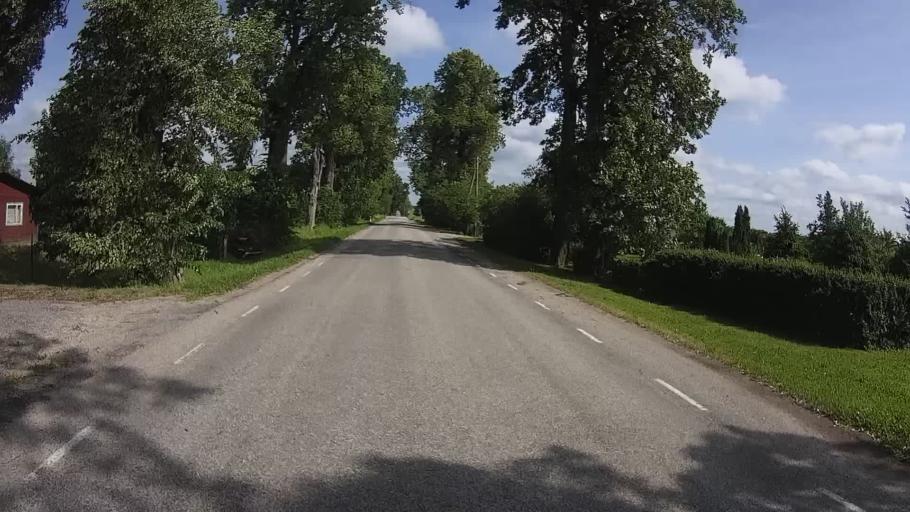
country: EE
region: Vorumaa
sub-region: Antsla vald
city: Vana-Antsla
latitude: 57.8656
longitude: 26.6086
